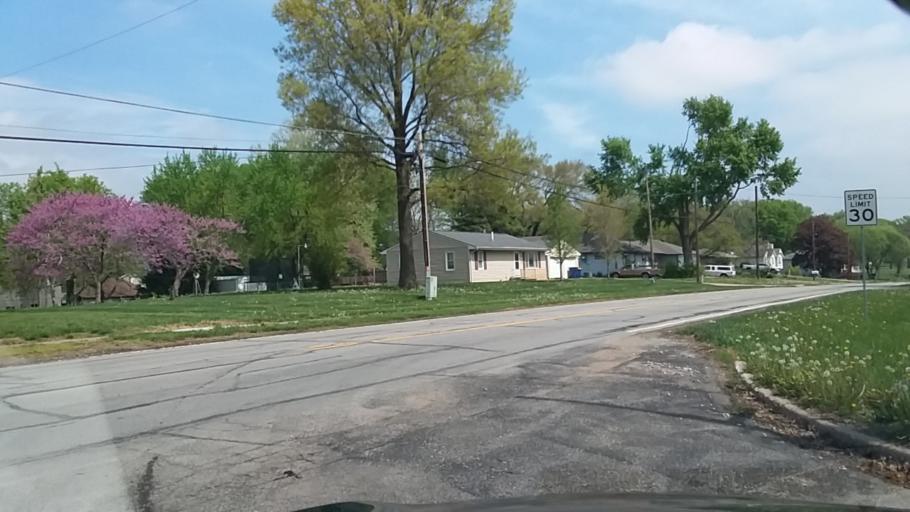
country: US
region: Kansas
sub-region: Johnson County
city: De Soto
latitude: 38.9739
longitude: -94.9804
